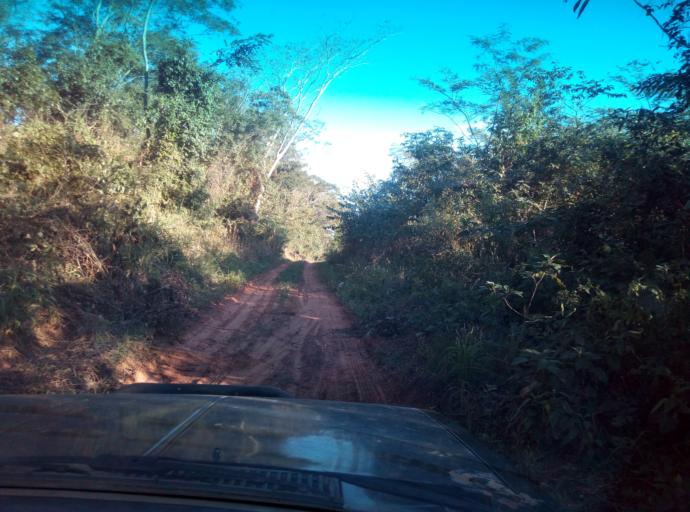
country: PY
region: Caaguazu
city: Carayao
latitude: -25.1873
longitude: -56.2626
